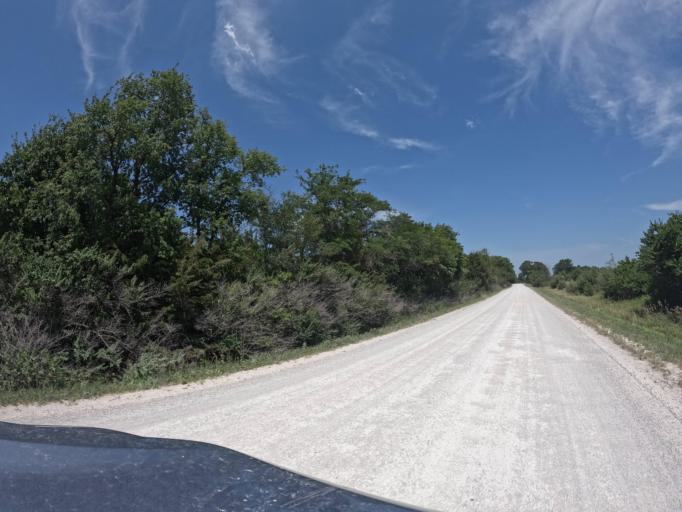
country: US
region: Iowa
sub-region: Henry County
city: Mount Pleasant
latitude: 40.9070
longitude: -91.5469
